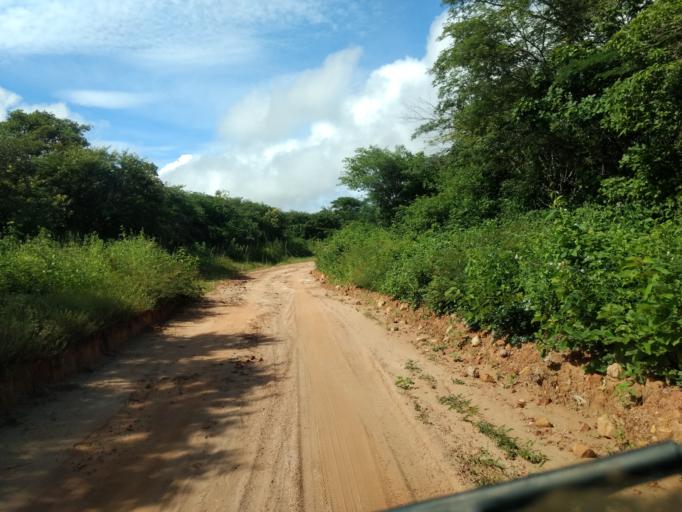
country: BR
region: Ceara
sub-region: Crateus
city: Crateus
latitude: -5.2178
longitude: -40.9474
